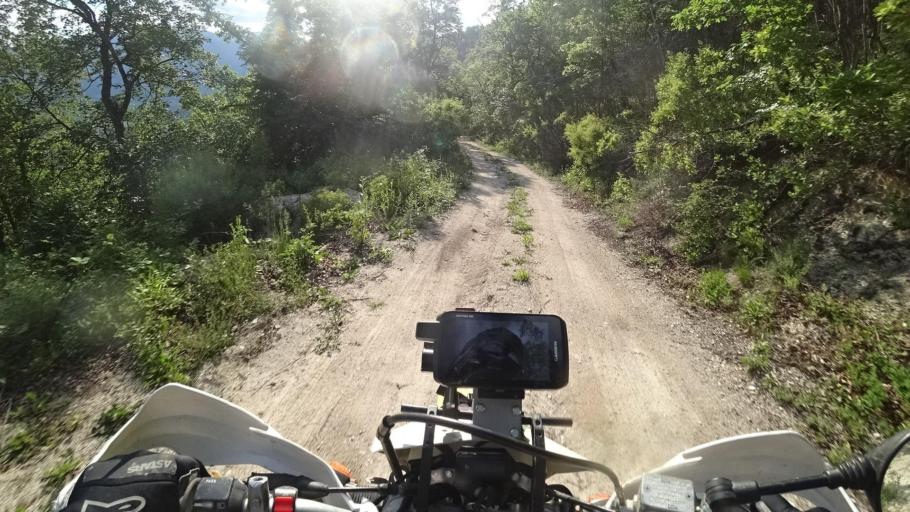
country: BA
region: Federation of Bosnia and Herzegovina
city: Sanica
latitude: 44.6272
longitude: 16.6838
